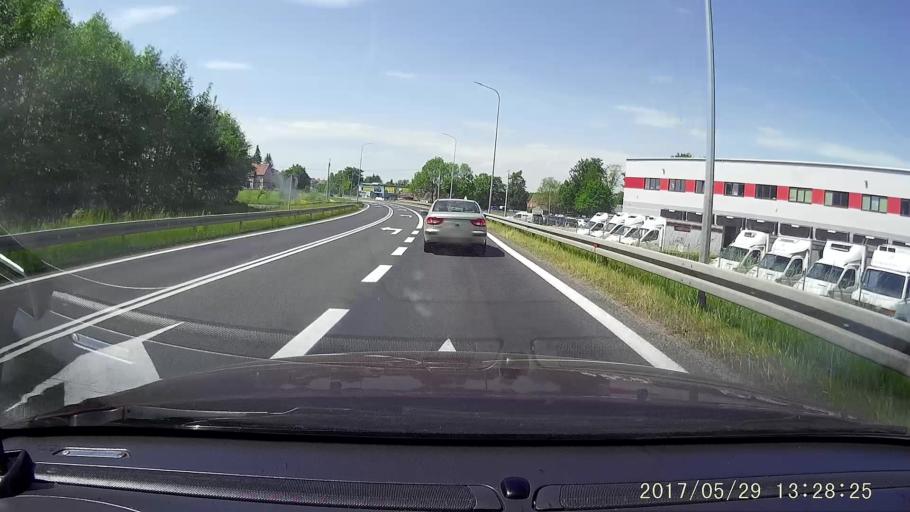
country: PL
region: Lower Silesian Voivodeship
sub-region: Powiat lubanski
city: Olszyna
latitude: 51.0643
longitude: 15.3727
